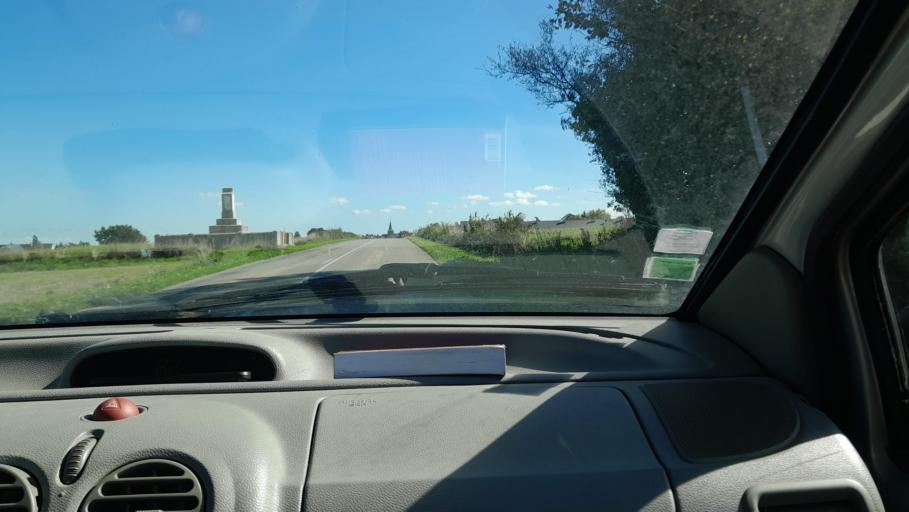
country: FR
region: Pays de la Loire
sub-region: Departement de la Mayenne
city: Quelaines-Saint-Gault
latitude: 47.9275
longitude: -0.8129
